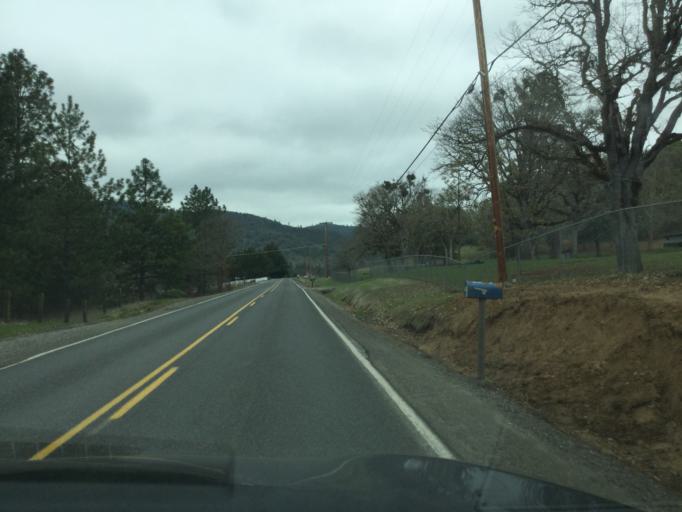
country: US
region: Oregon
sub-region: Jackson County
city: Gold Hill
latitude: 42.3981
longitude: -123.0144
